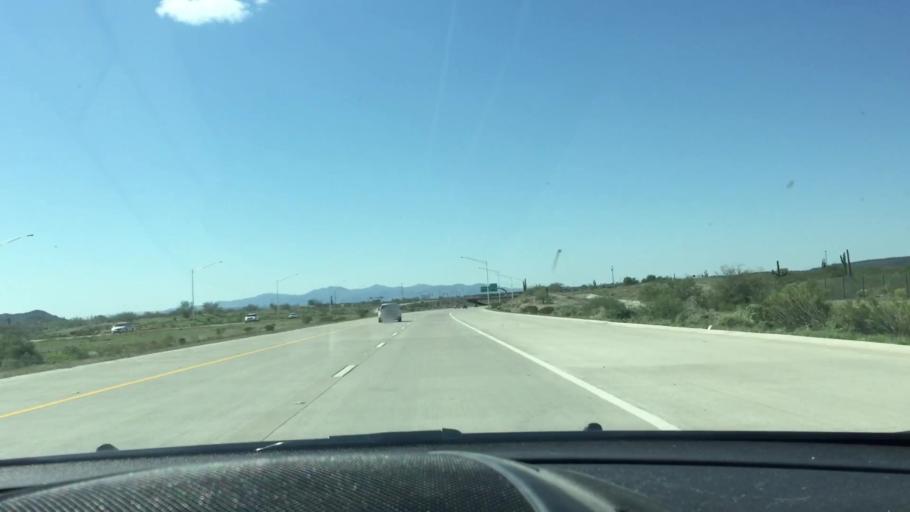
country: US
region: Arizona
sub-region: Maricopa County
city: Anthem
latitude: 33.7737
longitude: -112.2413
